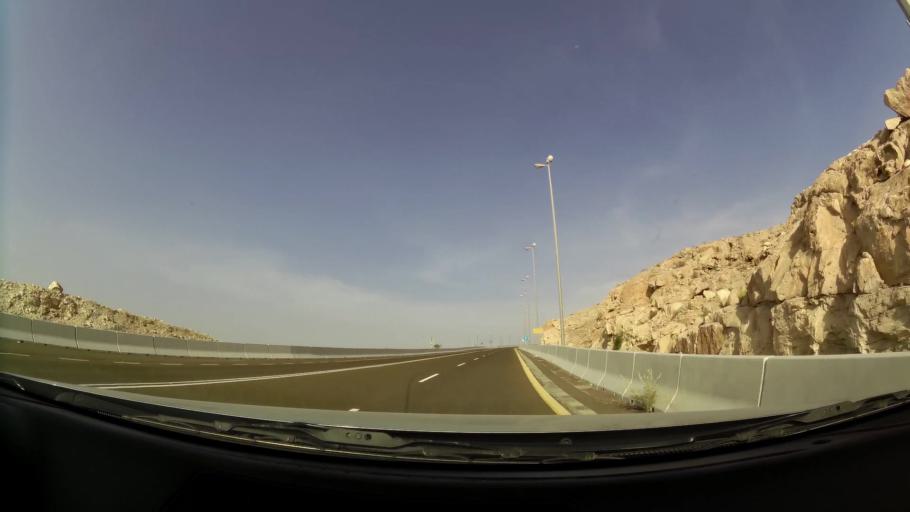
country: AE
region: Abu Dhabi
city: Al Ain
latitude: 24.0836
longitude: 55.7655
